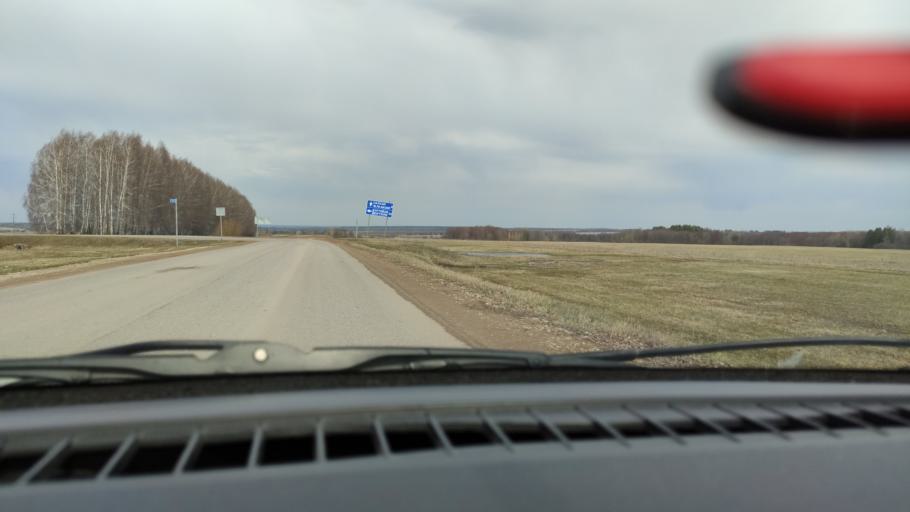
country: RU
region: Bashkortostan
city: Dyurtyuli
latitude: 55.6671
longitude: 55.0833
